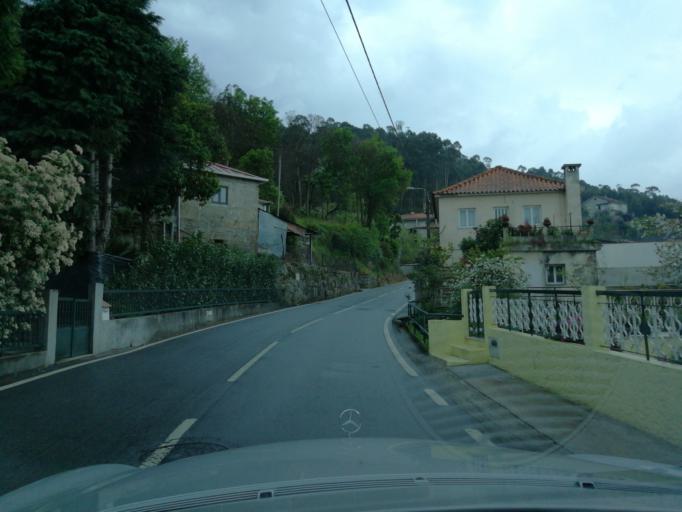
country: PT
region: Braga
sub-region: Braga
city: Oliveira
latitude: 41.4668
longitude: -8.4741
